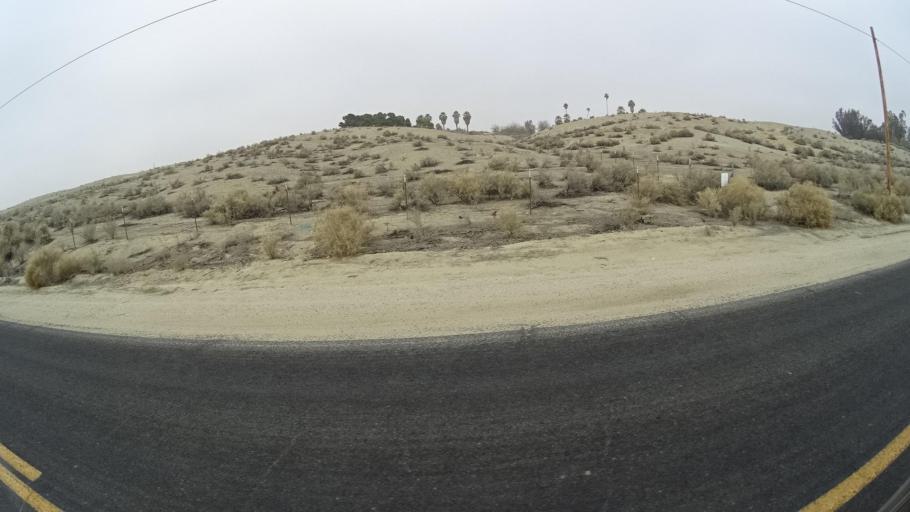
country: US
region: California
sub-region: Kern County
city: Ford City
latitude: 35.2340
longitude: -119.3316
